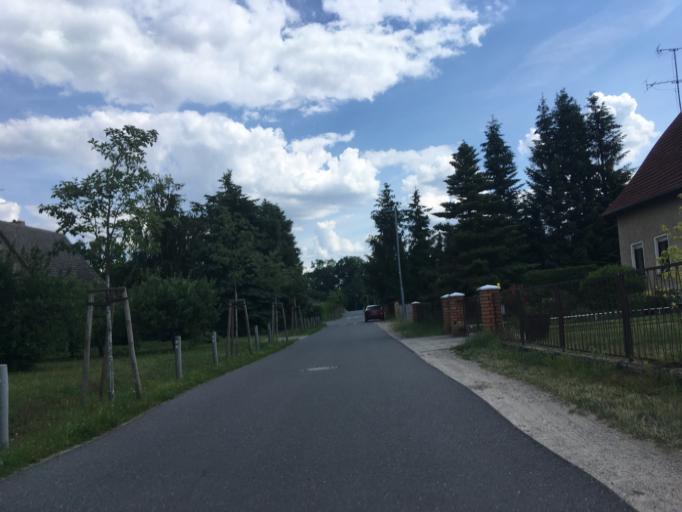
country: DE
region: Brandenburg
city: Muncheberg
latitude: 52.5026
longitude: 14.1090
